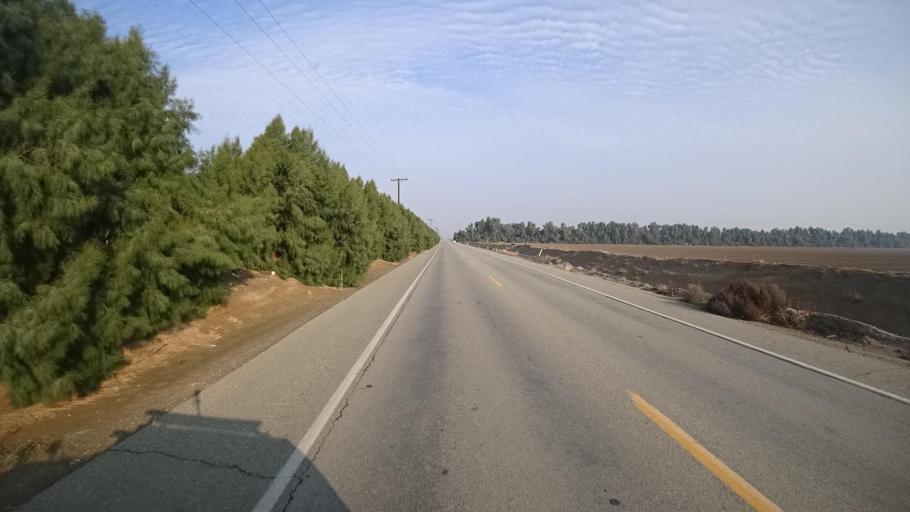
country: US
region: California
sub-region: Kern County
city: Weedpatch
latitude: 35.1336
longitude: -118.9147
